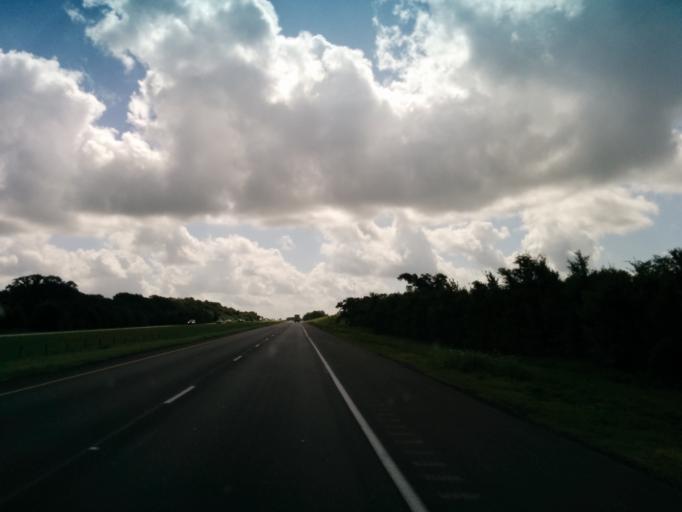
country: US
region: Texas
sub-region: Fayette County
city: Schulenburg
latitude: 29.6961
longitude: -96.8671
